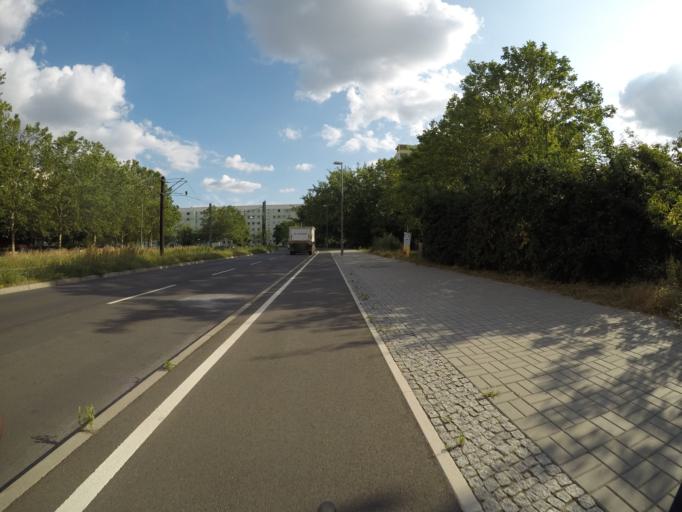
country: DE
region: Berlin
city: Marzahn
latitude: 52.5466
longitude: 13.5860
